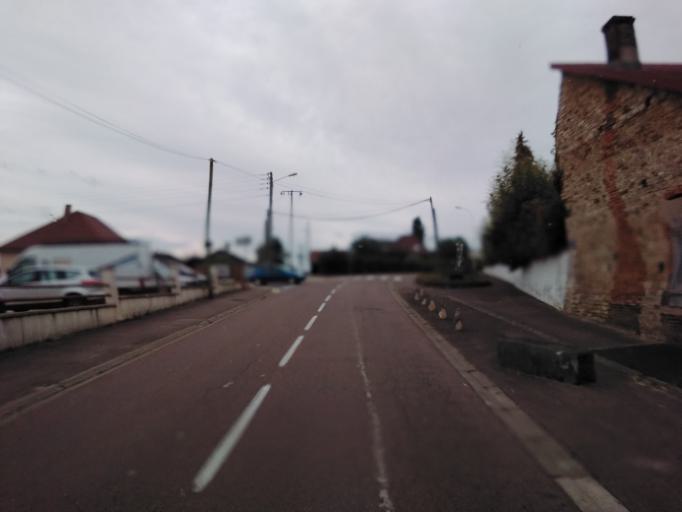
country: FR
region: Champagne-Ardenne
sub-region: Departement de l'Aube
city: Vendeuvre-sur-Barse
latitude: 48.2344
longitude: 4.4639
